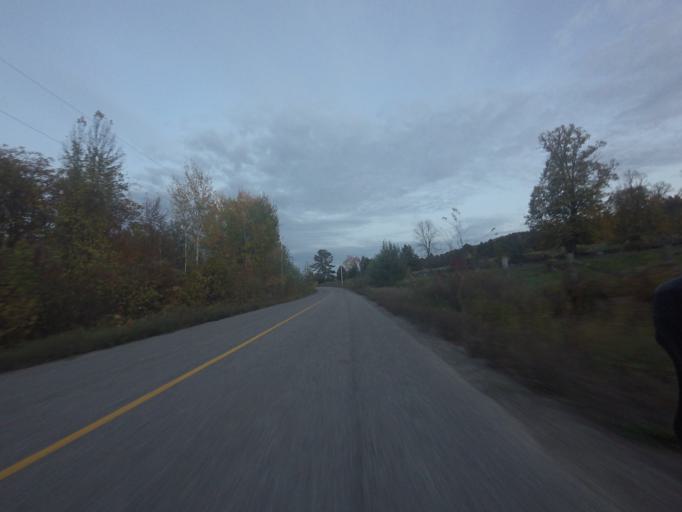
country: CA
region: Ontario
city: Renfrew
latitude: 45.3454
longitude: -76.9342
